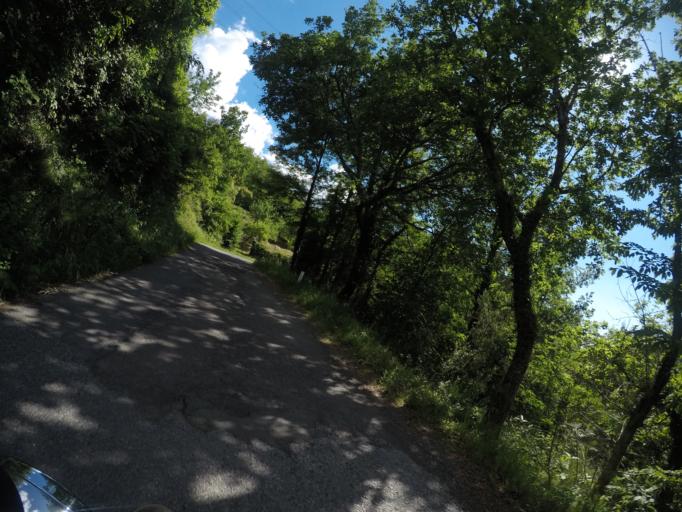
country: IT
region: Tuscany
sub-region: Provincia di Massa-Carrara
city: Casola in Lunigiana
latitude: 44.1769
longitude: 10.1518
